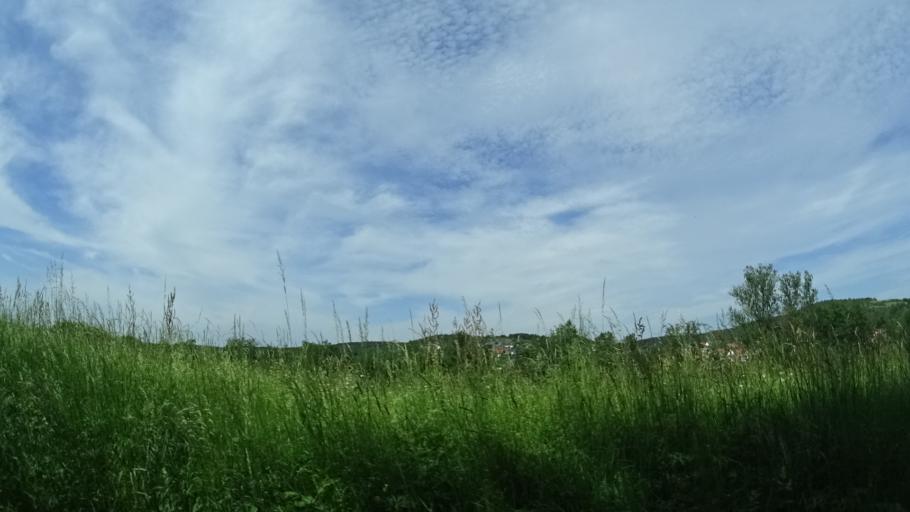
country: DE
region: Bavaria
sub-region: Regierungsbezirk Unterfranken
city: Karbach
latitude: 49.8647
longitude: 9.6310
